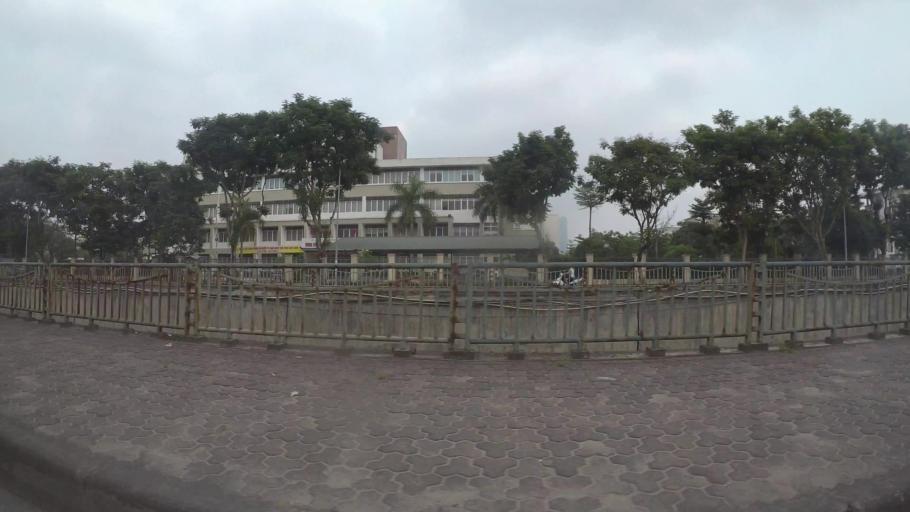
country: VN
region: Ha Noi
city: Cau Dien
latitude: 21.0268
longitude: 105.7632
